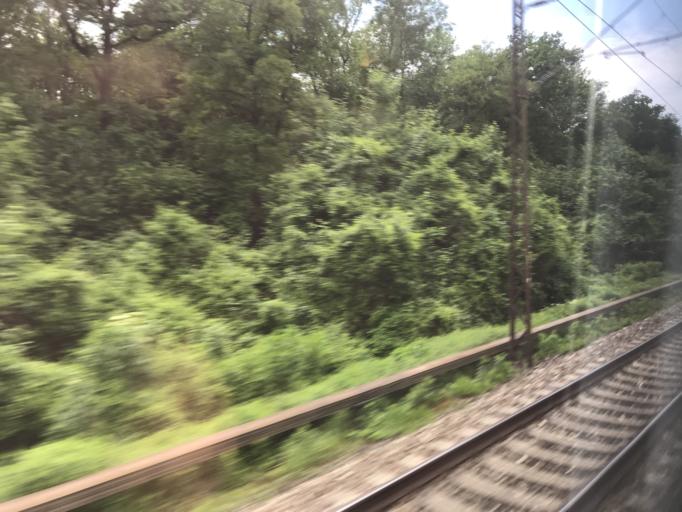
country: DE
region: Bavaria
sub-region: Swabia
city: Nersingen
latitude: 48.4197
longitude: 10.0922
